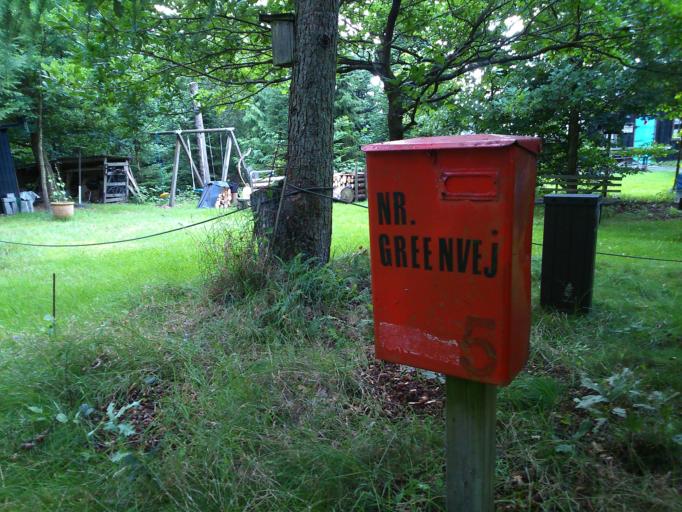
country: DK
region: Central Jutland
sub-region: Herning Kommune
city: Lind
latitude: 56.0031
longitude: 8.9779
